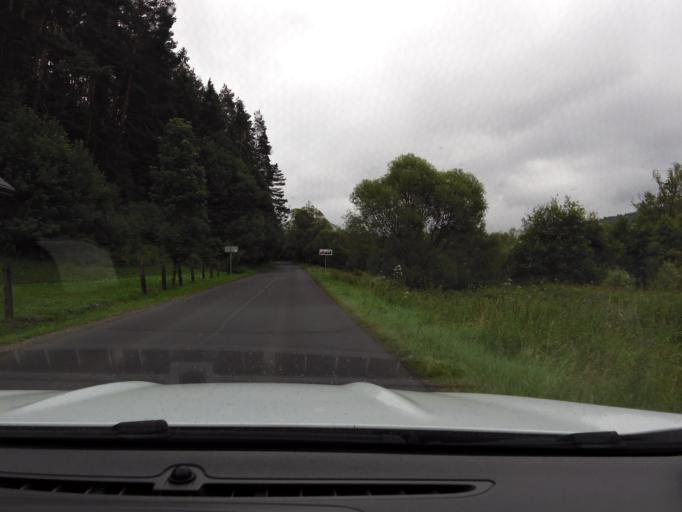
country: PL
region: Silesian Voivodeship
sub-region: Powiat zywiecki
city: Rajcza
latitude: 49.4934
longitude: 19.1119
